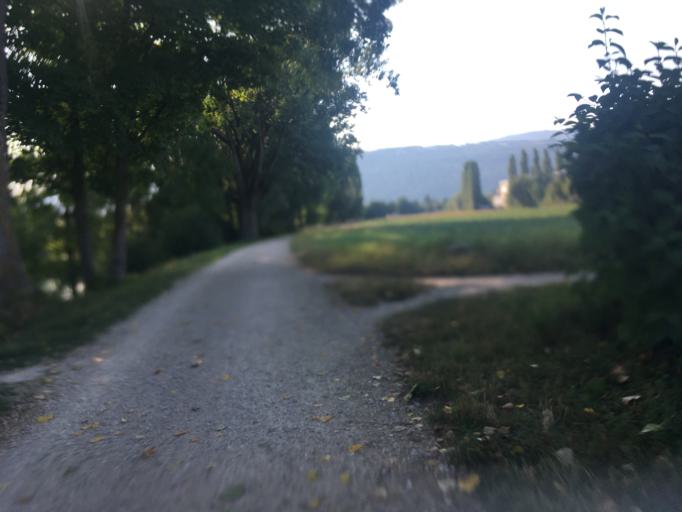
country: CH
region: Bern
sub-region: Biel/Bienne District
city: Brugg
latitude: 47.1169
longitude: 7.2648
